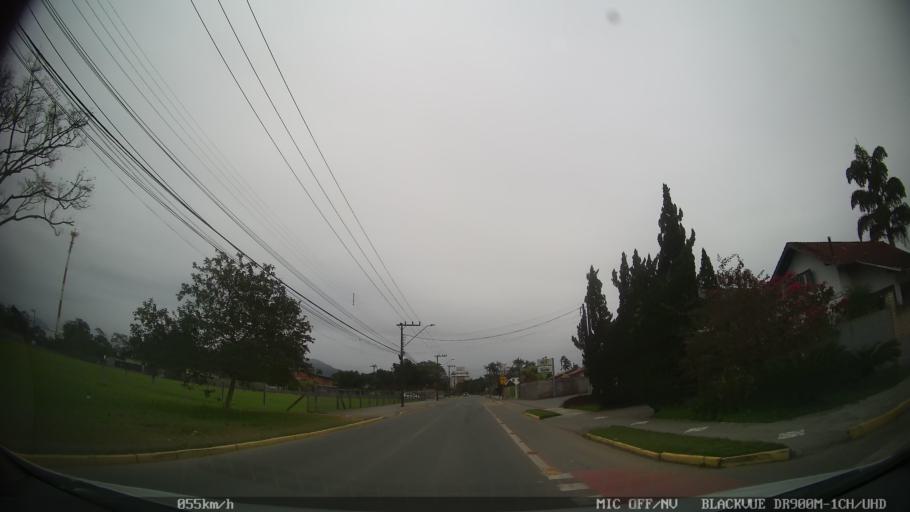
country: BR
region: Santa Catarina
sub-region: Joinville
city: Joinville
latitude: -26.2033
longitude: -48.9075
